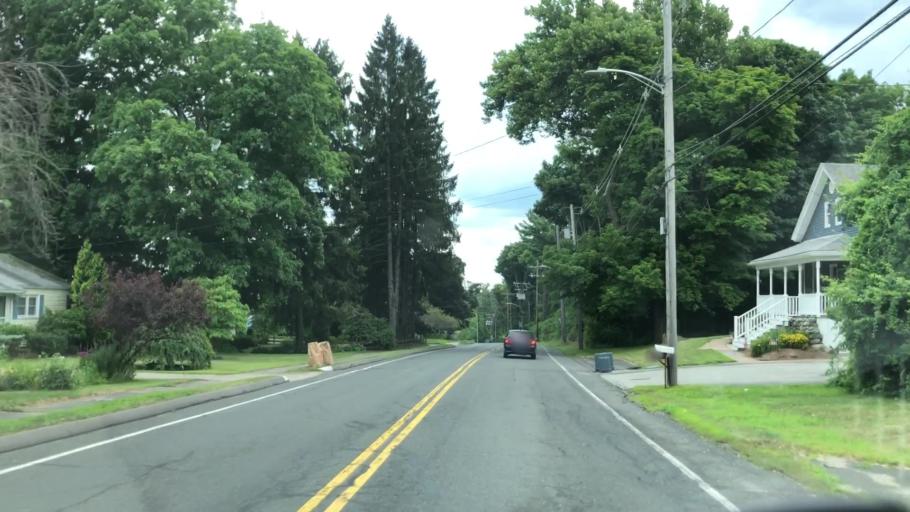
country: US
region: Massachusetts
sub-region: Hampden County
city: Holyoke
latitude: 42.1900
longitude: -72.6494
